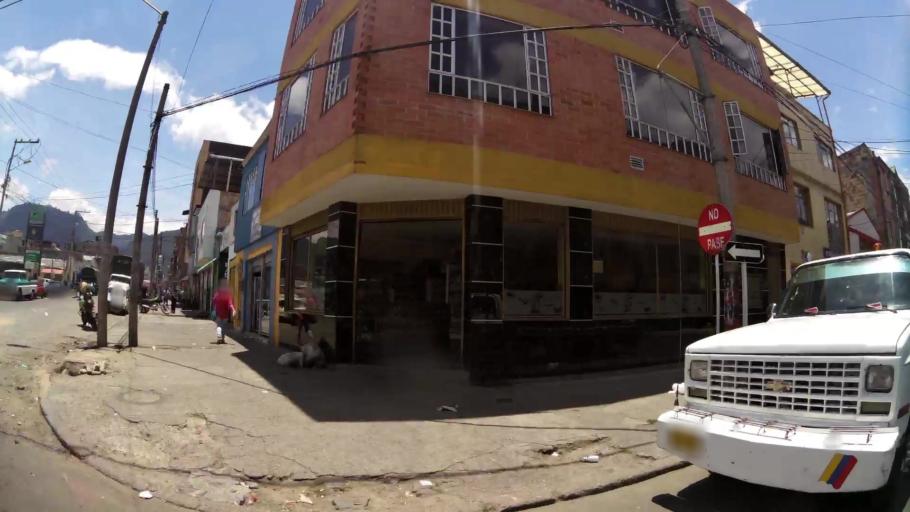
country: CO
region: Bogota D.C.
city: Bogota
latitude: 4.5972
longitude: -74.0881
